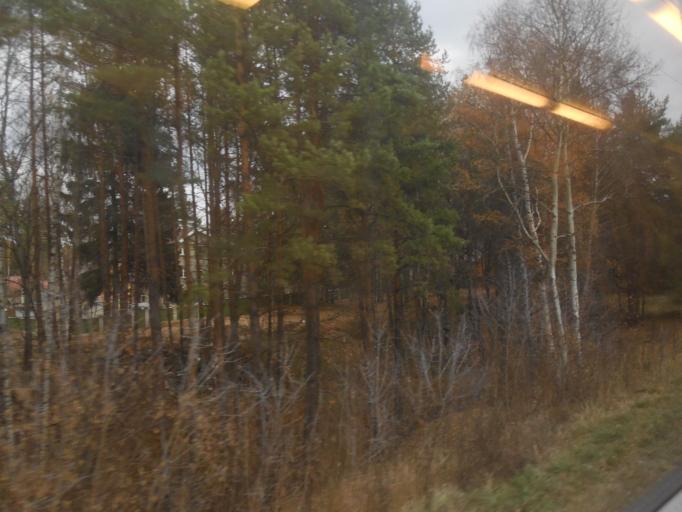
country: RU
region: Moskovskaya
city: Kratovo
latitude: 55.5858
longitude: 38.1757
